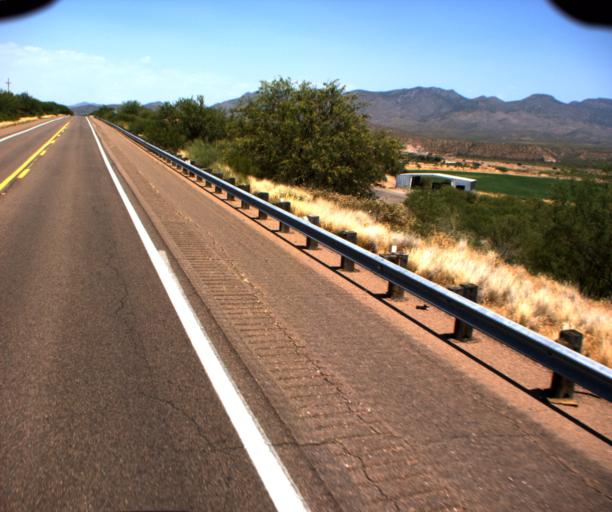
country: US
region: Arizona
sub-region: Gila County
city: Tonto Basin
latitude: 33.9247
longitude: -111.3173
